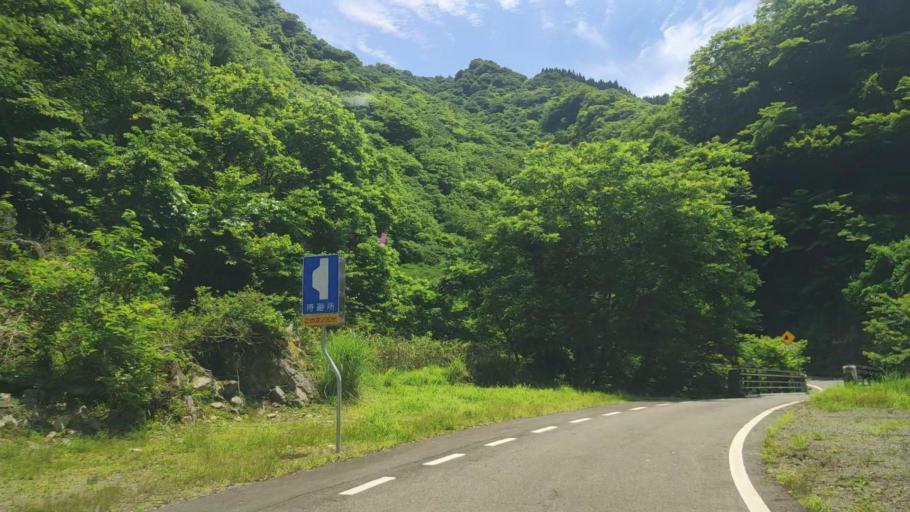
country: JP
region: Tottori
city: Tottori
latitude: 35.4066
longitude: 134.5070
